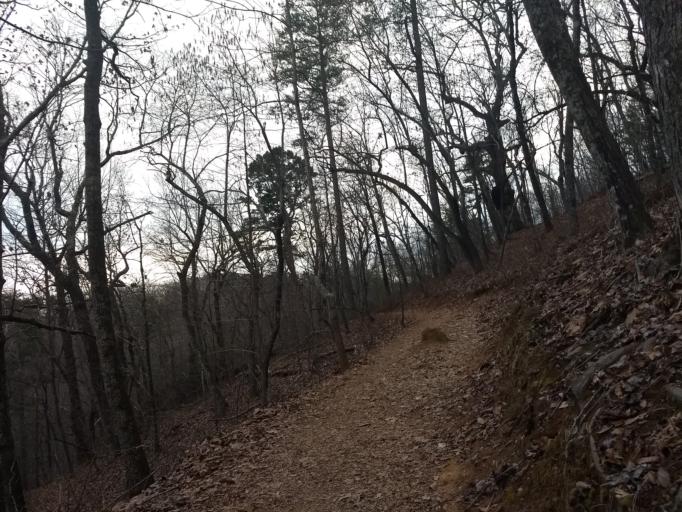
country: US
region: South Carolina
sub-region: Greenville County
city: Travelers Rest
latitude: 34.9426
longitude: -82.3917
